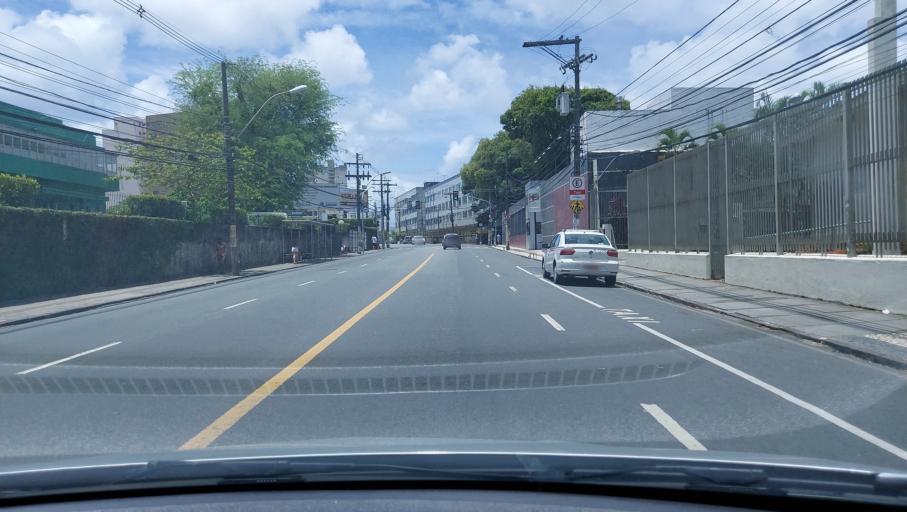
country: BR
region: Bahia
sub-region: Salvador
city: Salvador
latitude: -12.9904
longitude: -38.4883
